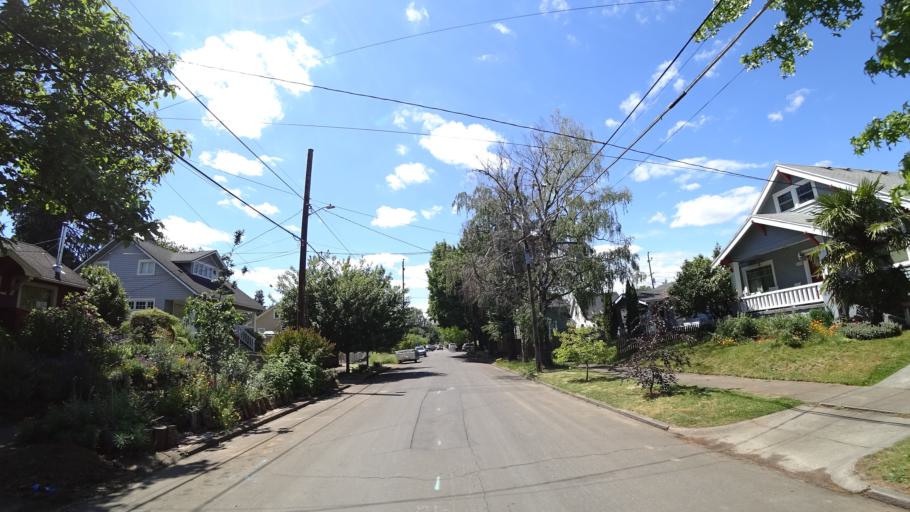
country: US
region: Oregon
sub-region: Multnomah County
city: Portland
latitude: 45.5613
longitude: -122.6840
